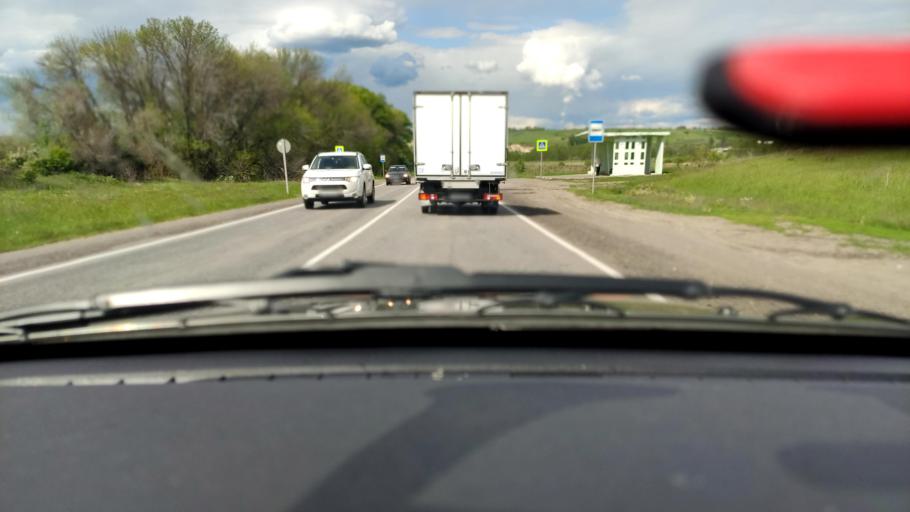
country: RU
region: Voronezj
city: Uryv-Pokrovka
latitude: 51.1256
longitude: 39.0391
